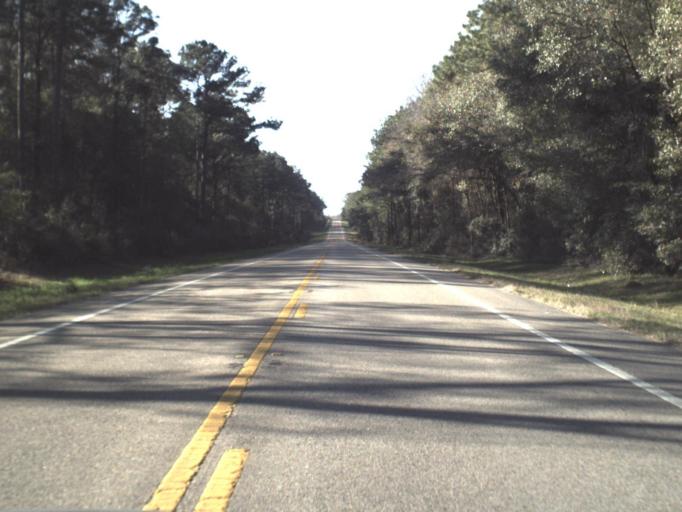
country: US
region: Florida
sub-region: Jackson County
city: Marianna
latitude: 30.6449
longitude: -85.2026
